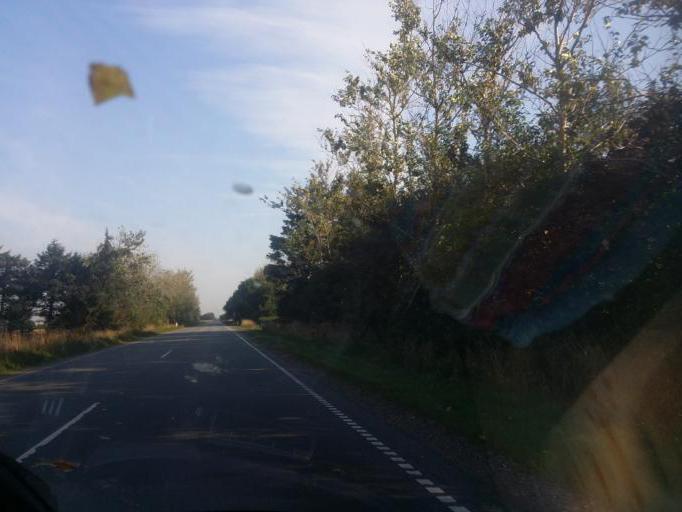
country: DK
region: South Denmark
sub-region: Tonder Kommune
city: Sherrebek
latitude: 55.0731
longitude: 8.8275
